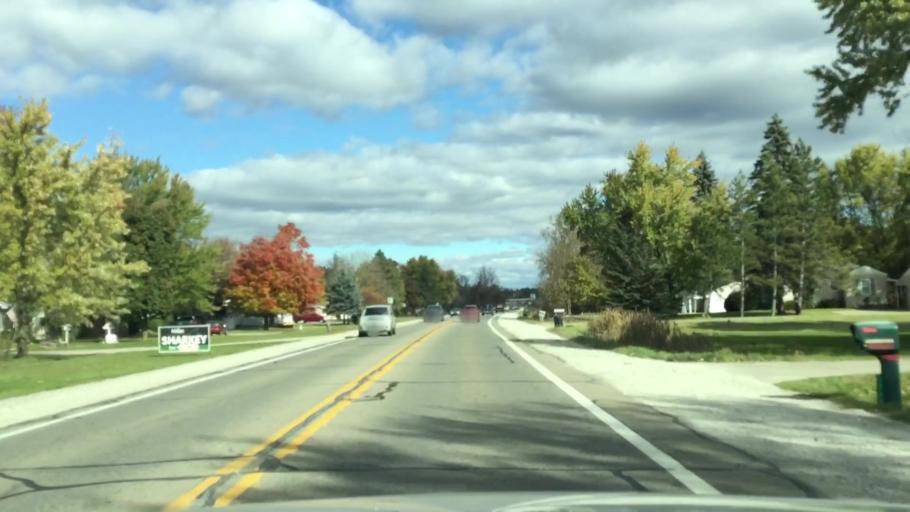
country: US
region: Michigan
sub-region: Lapeer County
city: Lapeer
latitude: 43.0758
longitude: -83.3147
